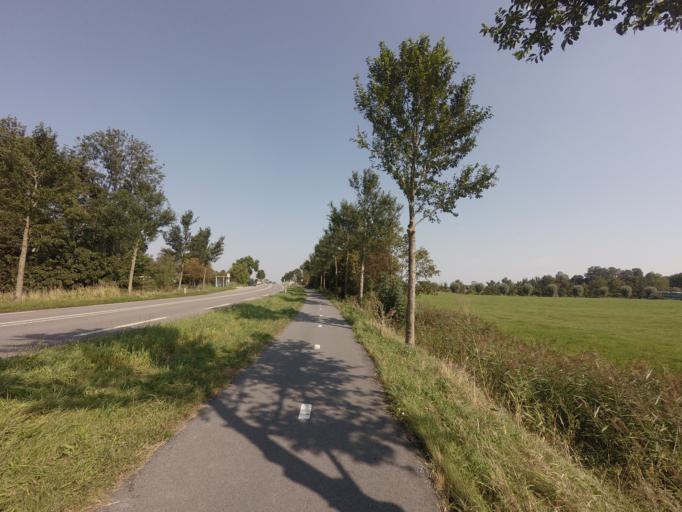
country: NL
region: Groningen
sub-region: Gemeente Zuidhorn
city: Grijpskerk
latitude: 53.2656
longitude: 6.3414
